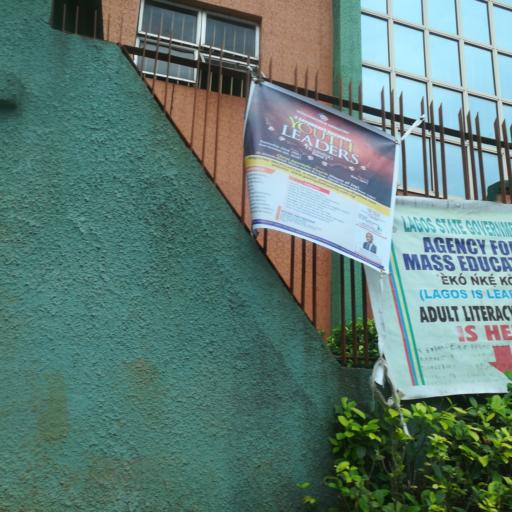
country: NG
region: Lagos
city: Agege
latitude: 6.6051
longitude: 3.2964
